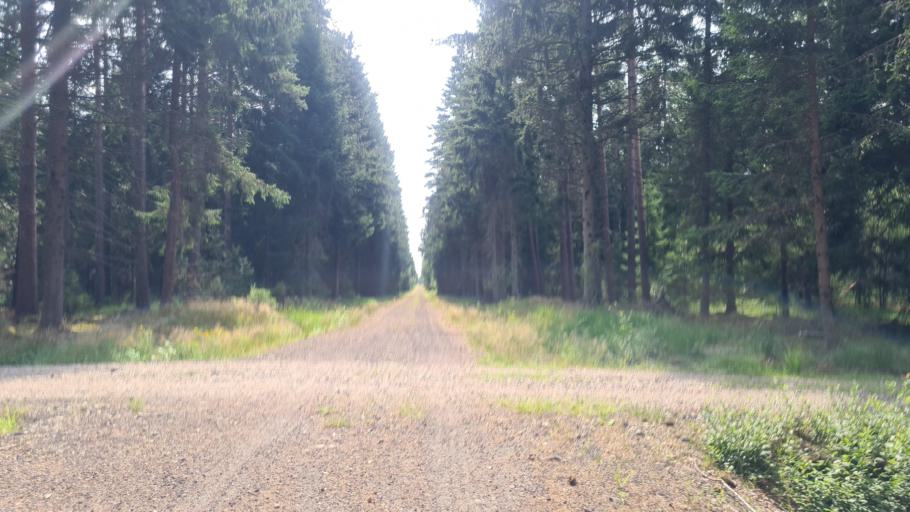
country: SE
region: Kronoberg
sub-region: Ljungby Kommun
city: Lagan
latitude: 56.9531
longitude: 13.9600
